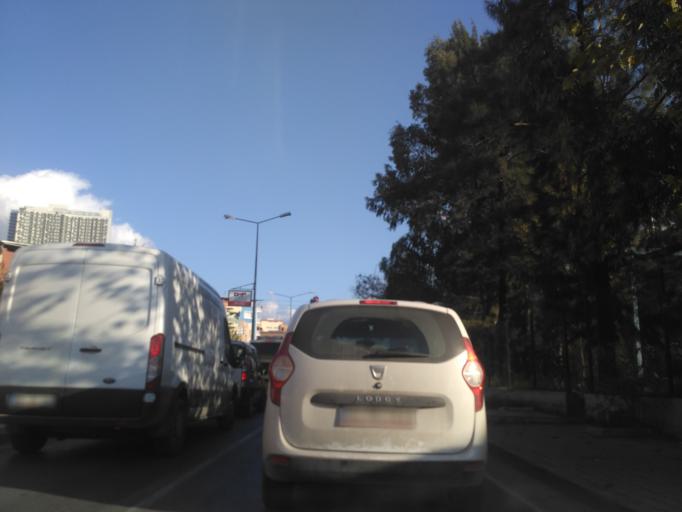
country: TR
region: Izmir
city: Buca
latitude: 38.4296
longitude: 27.2026
